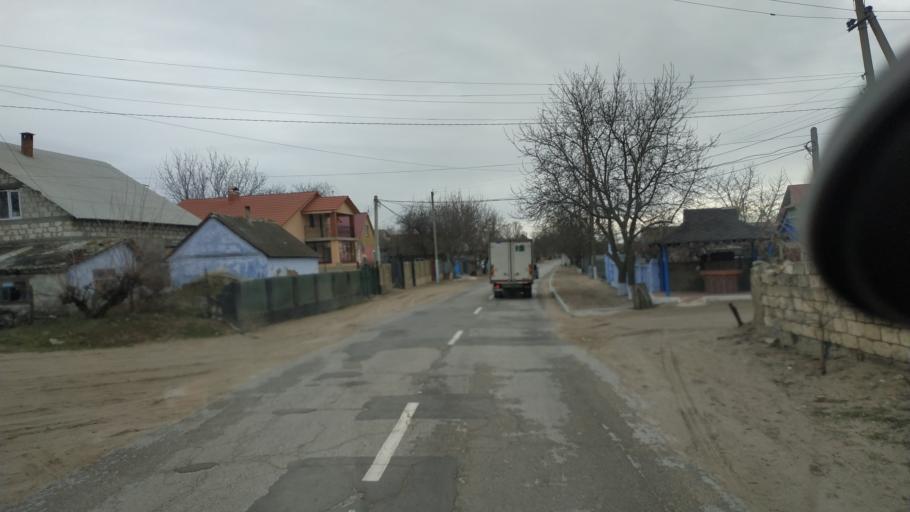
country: MD
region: Telenesti
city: Cocieri
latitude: 47.3170
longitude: 29.1034
